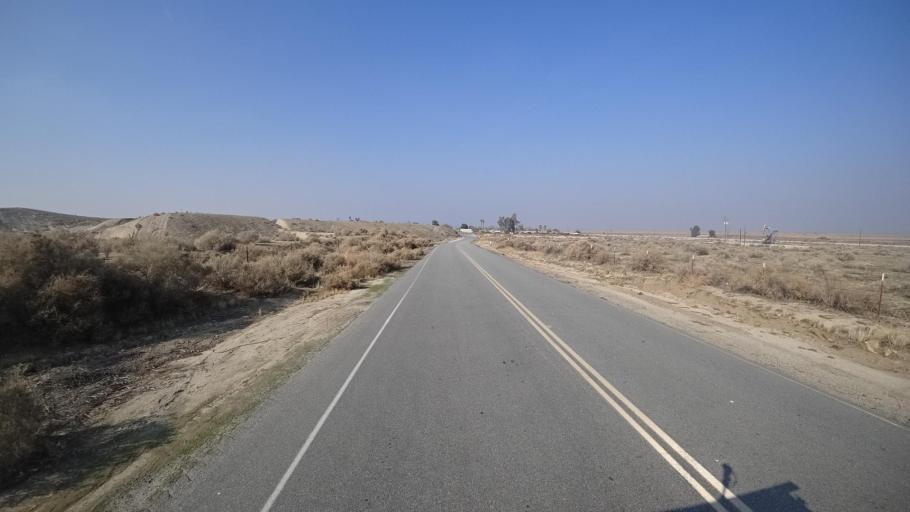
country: US
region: California
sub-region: Kern County
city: Buttonwillow
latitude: 35.2940
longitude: -119.3473
